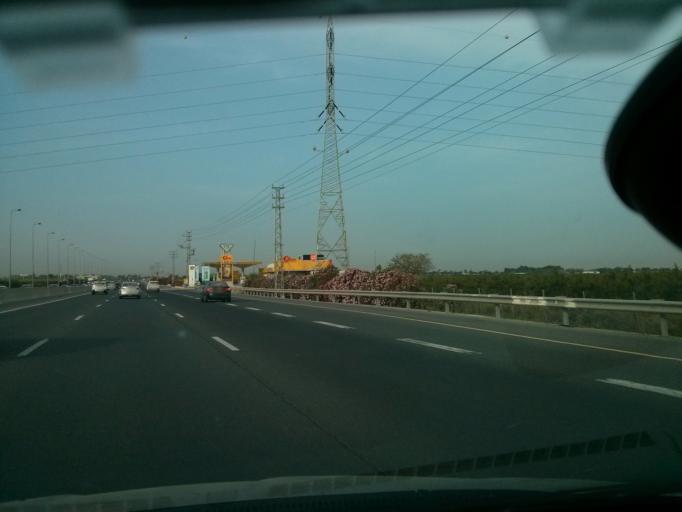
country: IL
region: Central District
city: Bene 'Ayish
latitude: 31.7571
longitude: 34.7817
